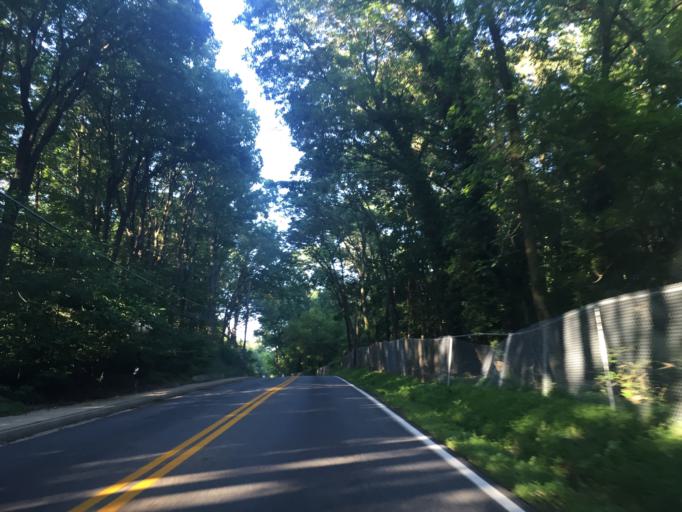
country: US
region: Maryland
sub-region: Baltimore County
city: Arbutus
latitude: 39.2448
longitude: -76.7114
